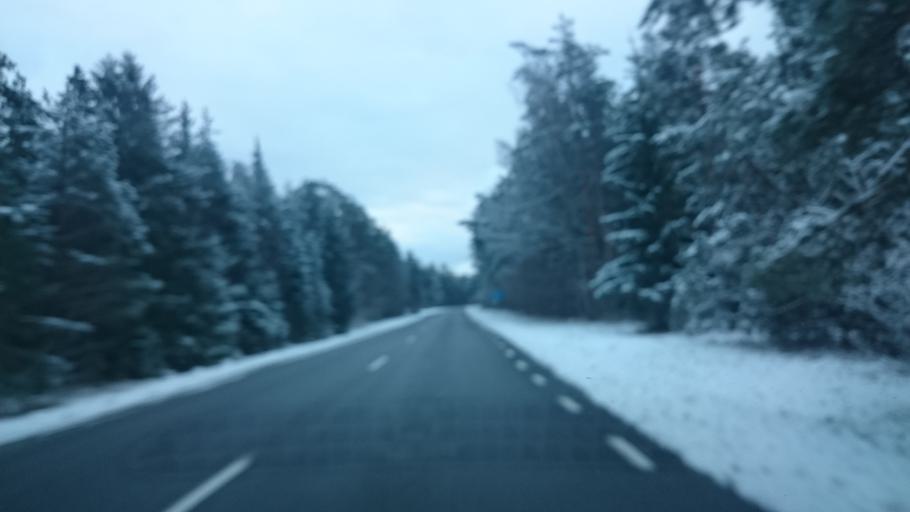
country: EE
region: Saare
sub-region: Kuressaare linn
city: Kuressaare
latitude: 58.3927
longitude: 22.6478
